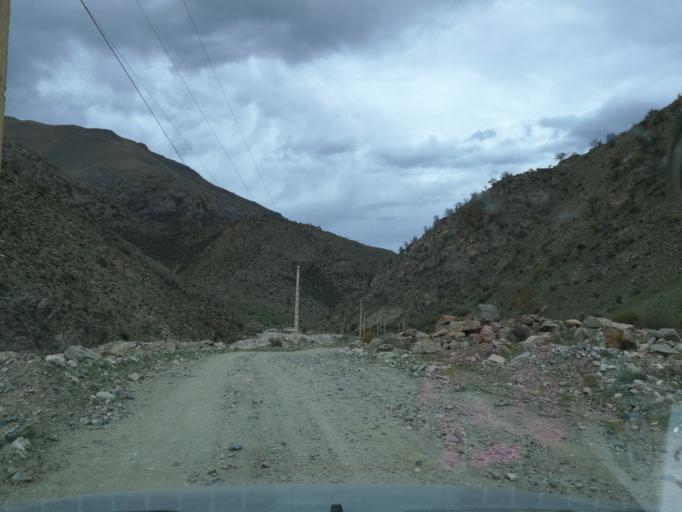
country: IR
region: Mazandaran
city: `Abbasabad
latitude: 36.4329
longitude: 51.0433
